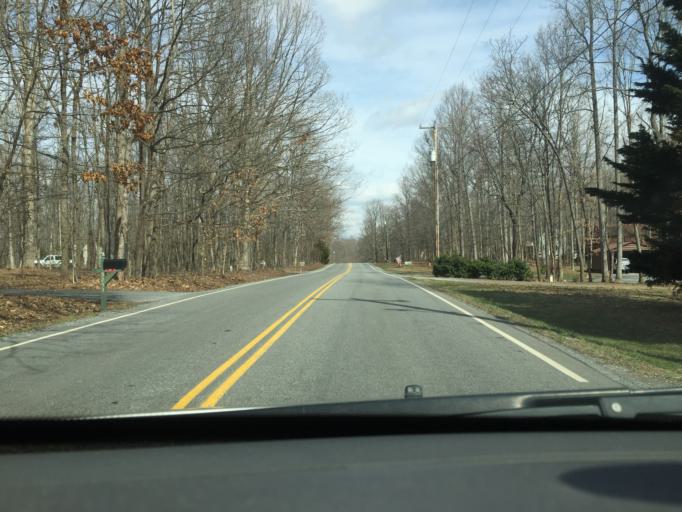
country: US
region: Virginia
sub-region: Bedford County
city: Forest
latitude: 37.3190
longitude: -79.3105
